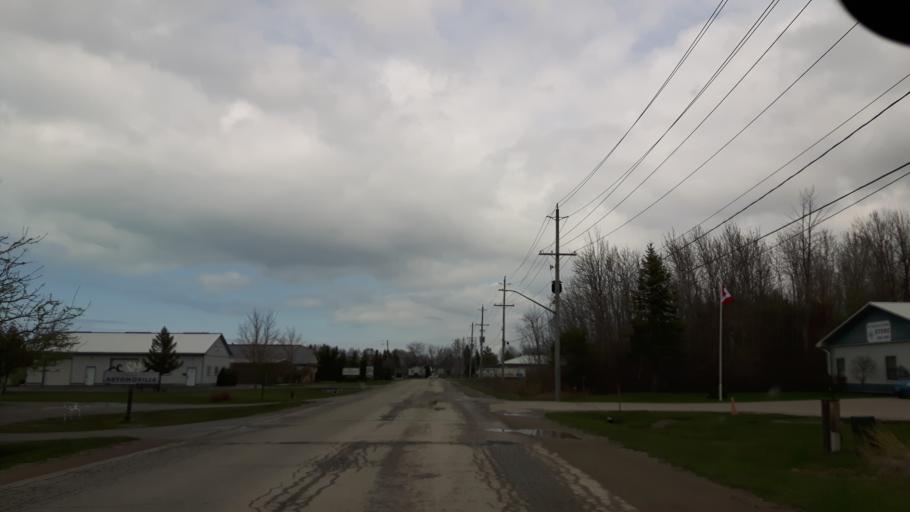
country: CA
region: Ontario
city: Goderich
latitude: 43.7287
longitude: -81.6994
